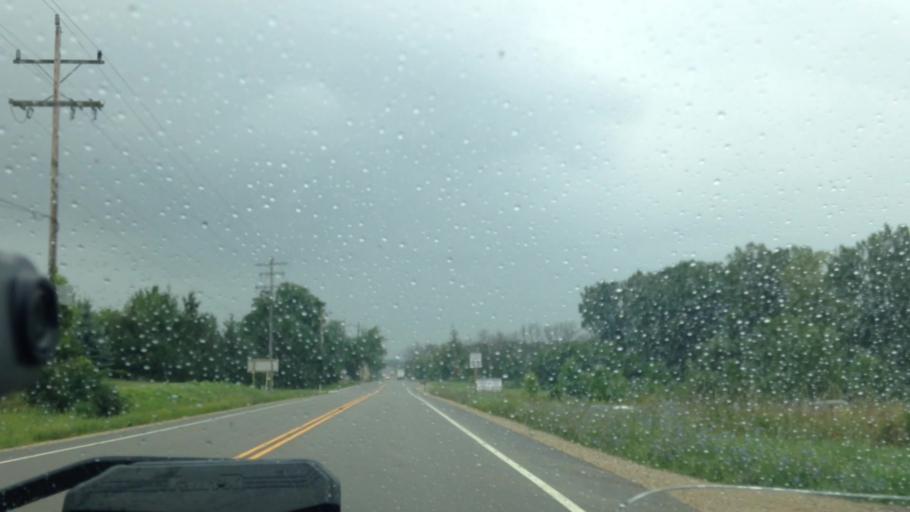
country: US
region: Wisconsin
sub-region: Washington County
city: Richfield
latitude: 43.2940
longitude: -88.2202
